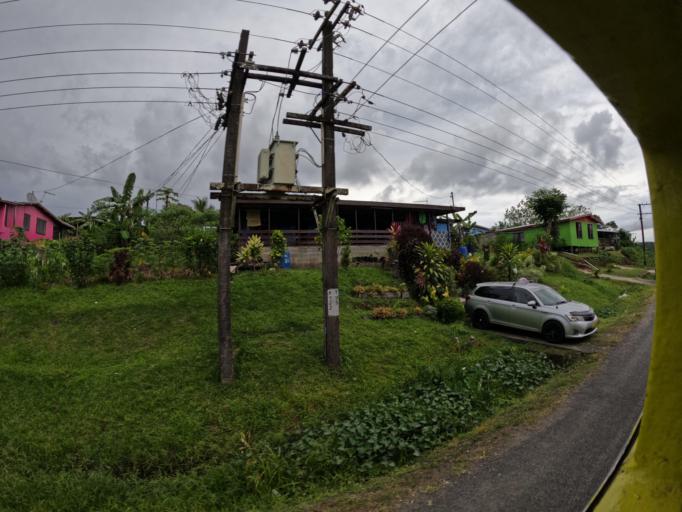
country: FJ
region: Central
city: Suva
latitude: -18.0763
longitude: 178.4596
